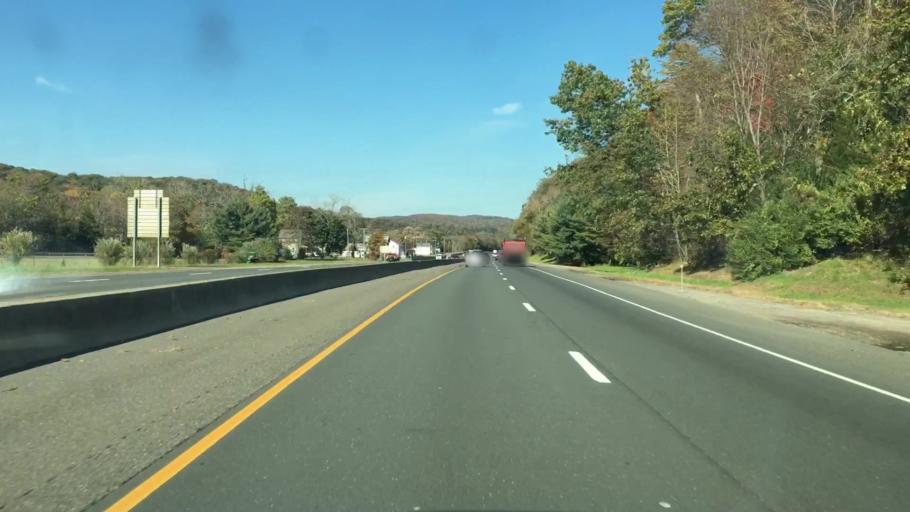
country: US
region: Connecticut
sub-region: New Haven County
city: Seymour
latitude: 41.4072
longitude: -73.0695
